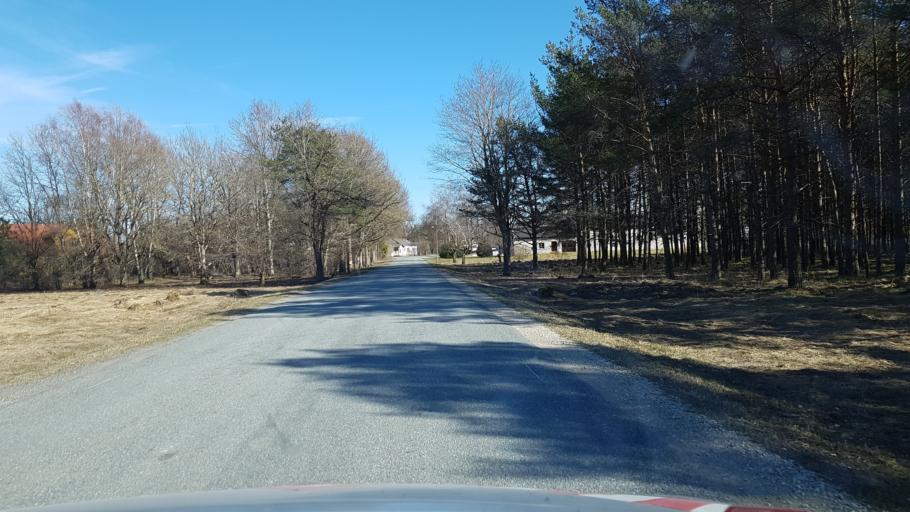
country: EE
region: Laeaene-Virumaa
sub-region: Rakke vald
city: Rakke
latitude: 59.0469
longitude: 26.3966
